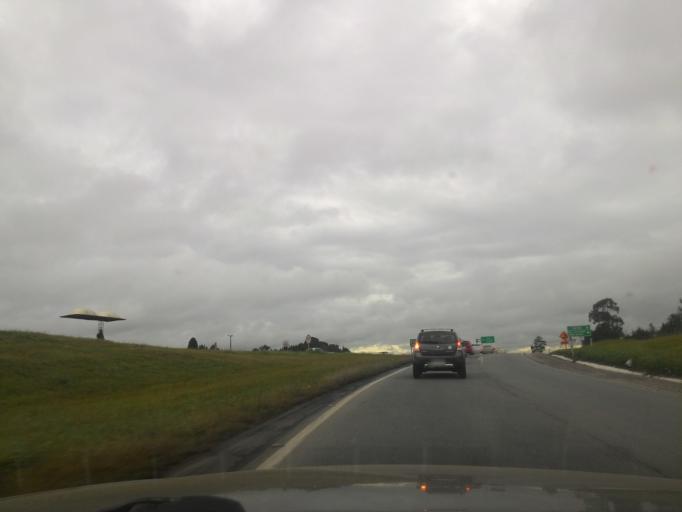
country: BR
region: Parana
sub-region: Sao Jose Dos Pinhais
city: Sao Jose dos Pinhais
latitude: -25.5420
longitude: -49.3106
